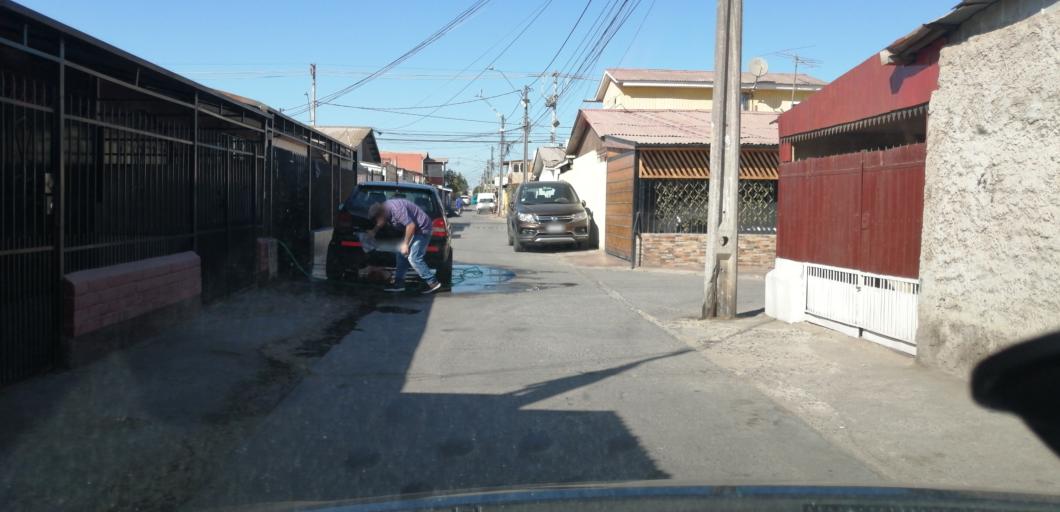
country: CL
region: Santiago Metropolitan
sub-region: Provincia de Santiago
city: Lo Prado
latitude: -33.4320
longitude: -70.7689
